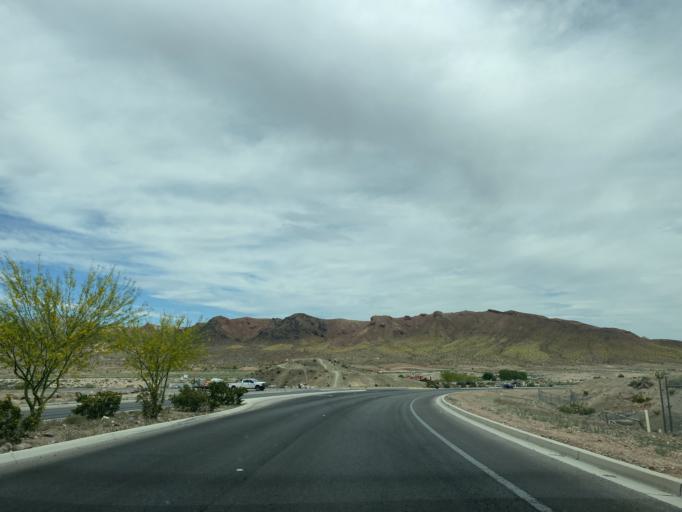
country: US
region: Nevada
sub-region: Clark County
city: Henderson
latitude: 36.0913
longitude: -114.9564
